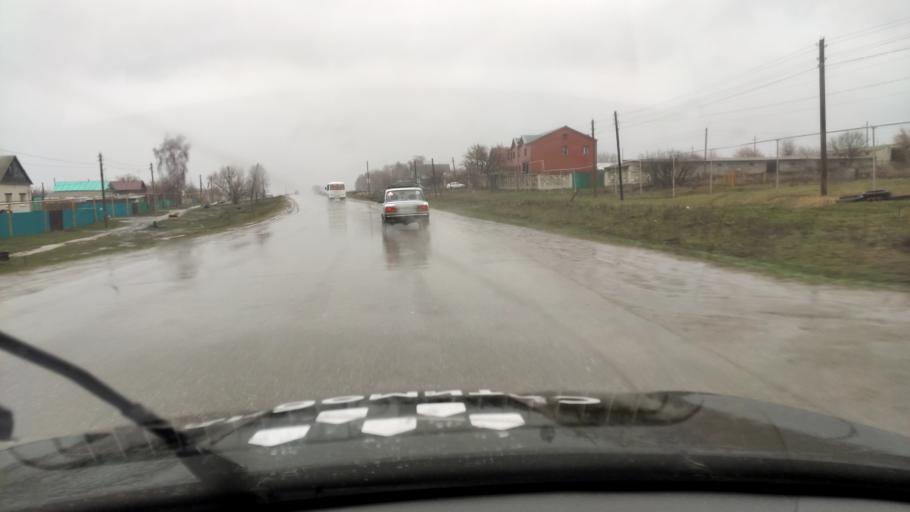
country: RU
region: Samara
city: Varlamovo
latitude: 53.2187
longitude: 48.2633
